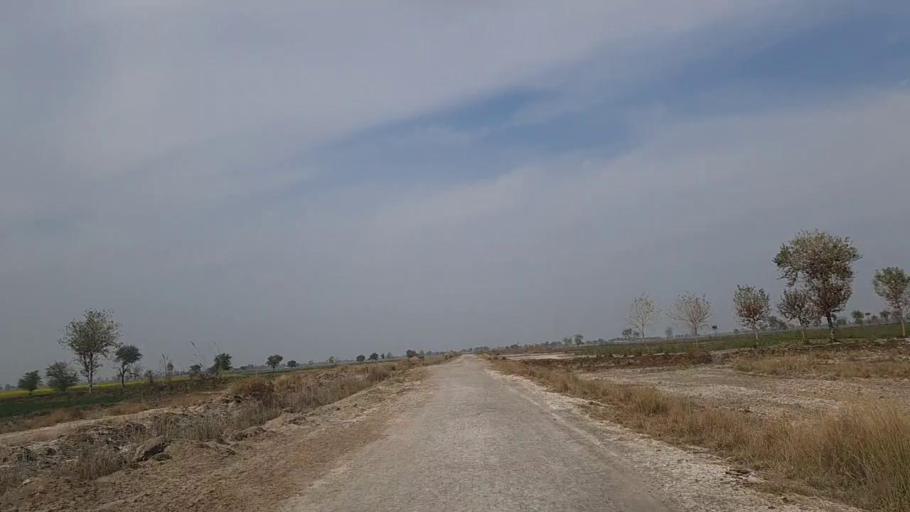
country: PK
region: Sindh
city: Daur
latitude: 26.4662
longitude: 68.4033
